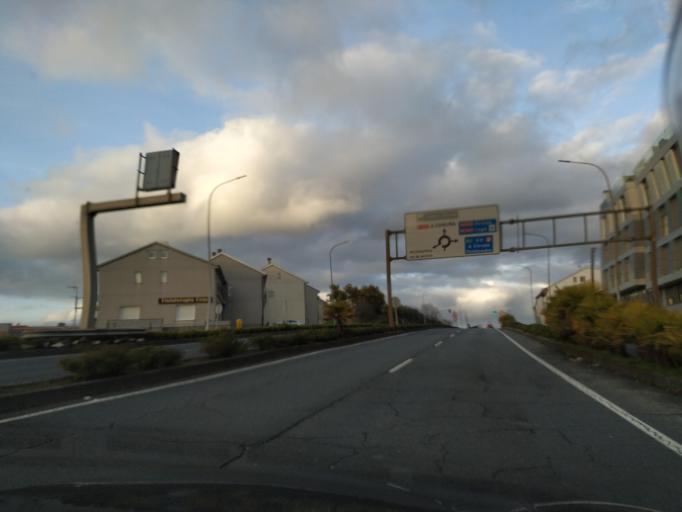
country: ES
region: Galicia
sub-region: Provincia da Coruna
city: Santiago de Compostela
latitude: 42.8969
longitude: -8.5297
